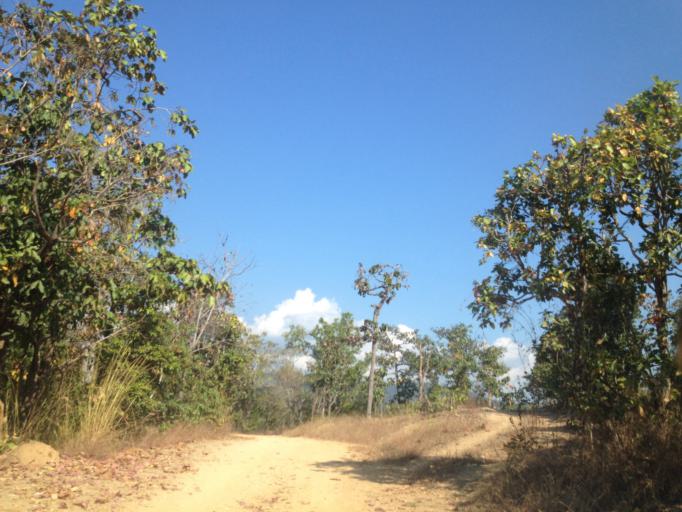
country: TH
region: Mae Hong Son
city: Ban Huai I Huak
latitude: 18.1183
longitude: 98.2072
